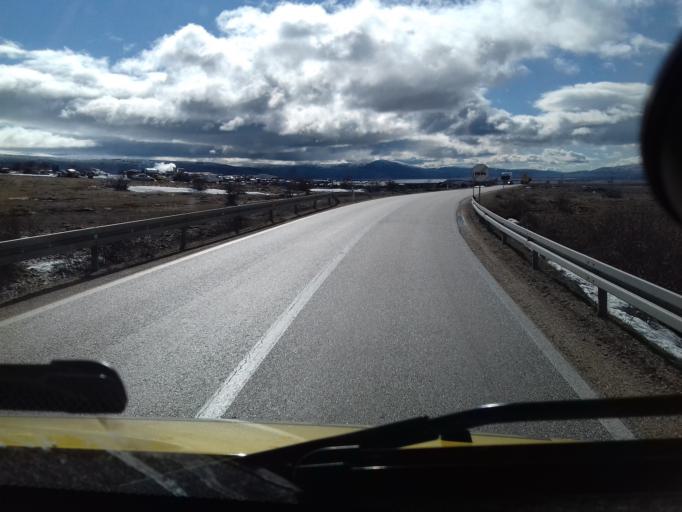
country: BA
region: Federation of Bosnia and Herzegovina
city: Tomislavgrad
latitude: 43.7733
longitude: 17.2331
